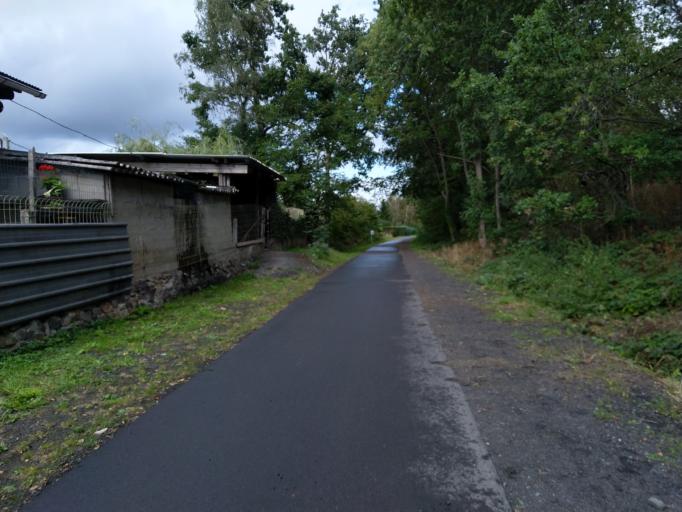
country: BE
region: Wallonia
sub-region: Province de Liege
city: Aubel
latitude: 50.6827
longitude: 5.8527
